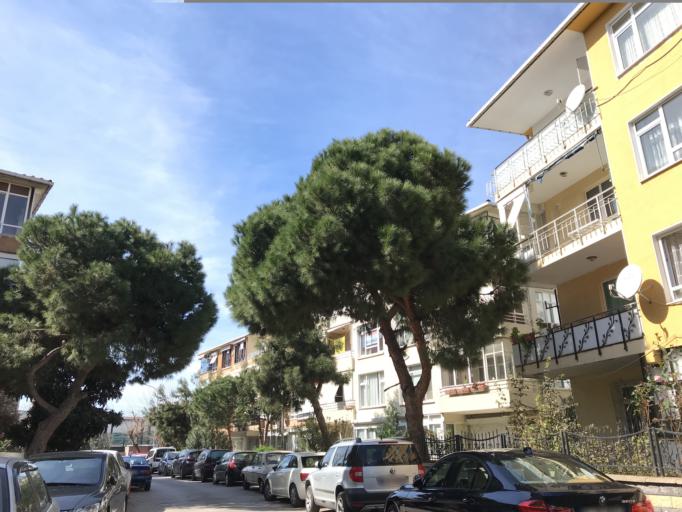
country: TR
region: Istanbul
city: Maltepe
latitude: 40.9269
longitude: 29.1257
